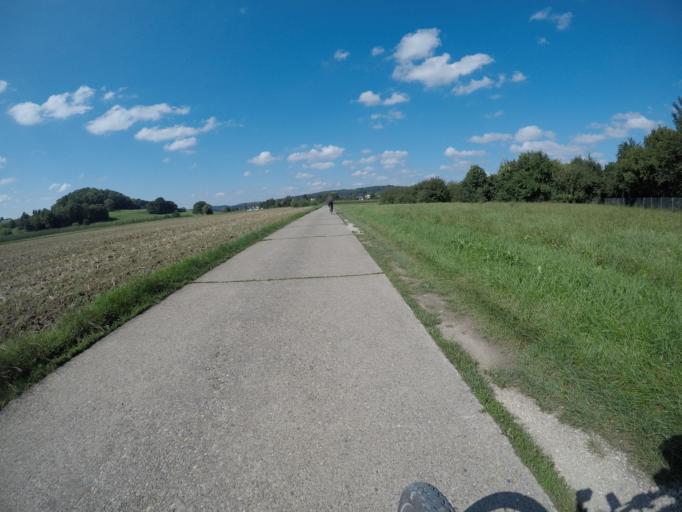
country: DE
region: Baden-Wuerttemberg
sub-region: Regierungsbezirk Stuttgart
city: Neckartailfingen
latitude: 48.6120
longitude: 9.2849
